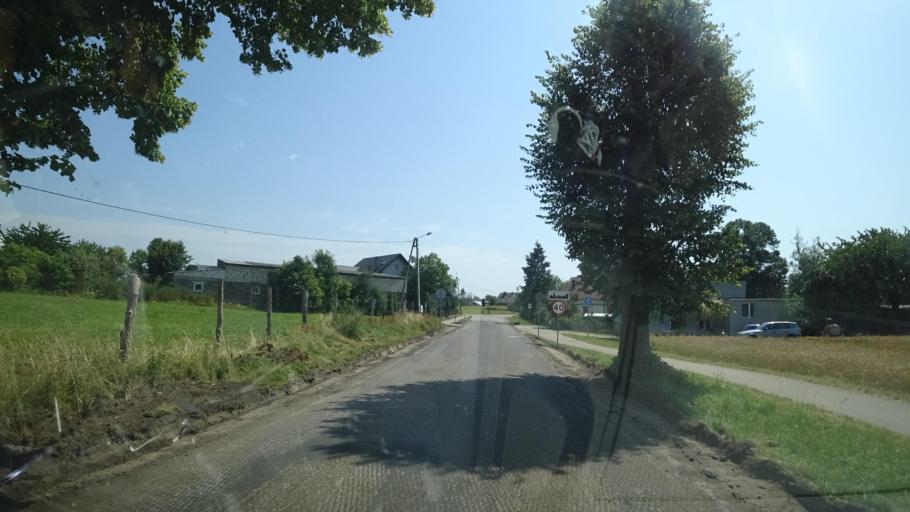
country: PL
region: Pomeranian Voivodeship
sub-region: Powiat chojnicki
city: Brusy
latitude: 53.8712
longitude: 17.6686
